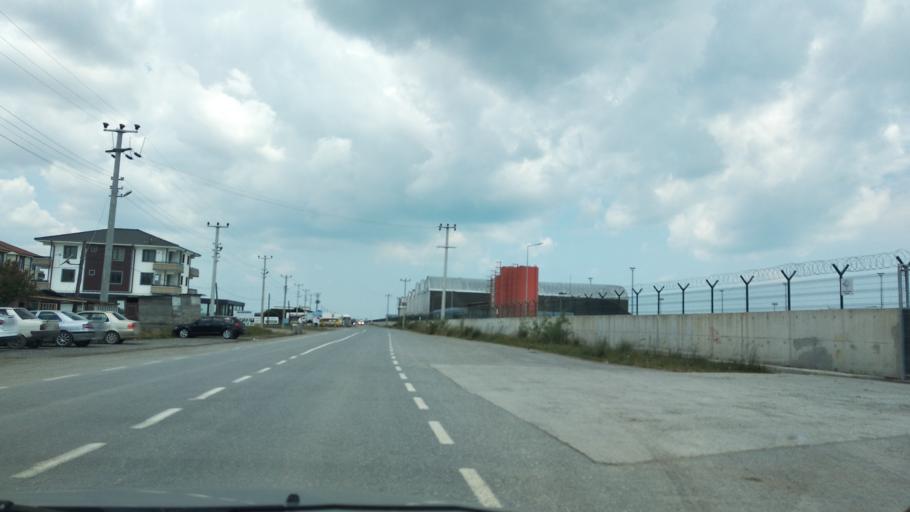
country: TR
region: Sakarya
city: Karasu
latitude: 41.1164
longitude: 30.6759
